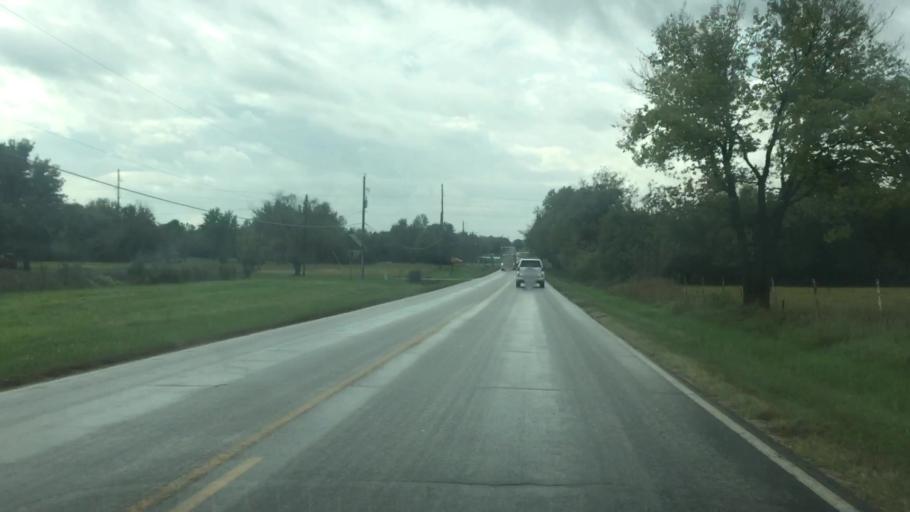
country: US
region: Kansas
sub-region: Allen County
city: Iola
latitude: 37.8953
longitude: -95.4095
